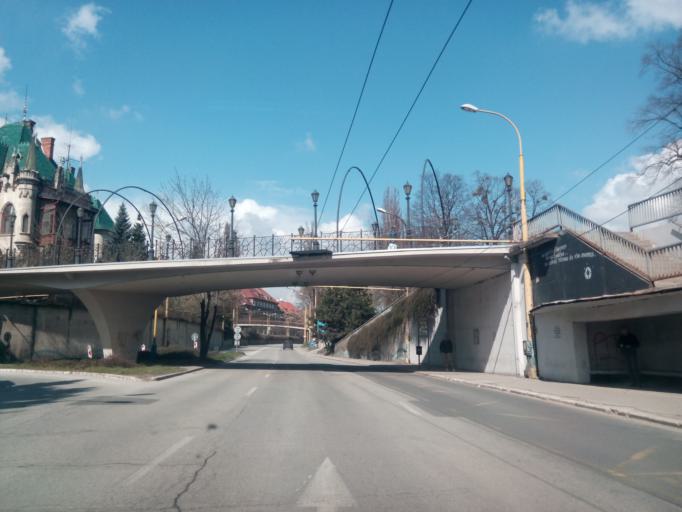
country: SK
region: Kosicky
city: Kosice
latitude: 48.7216
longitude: 21.2638
